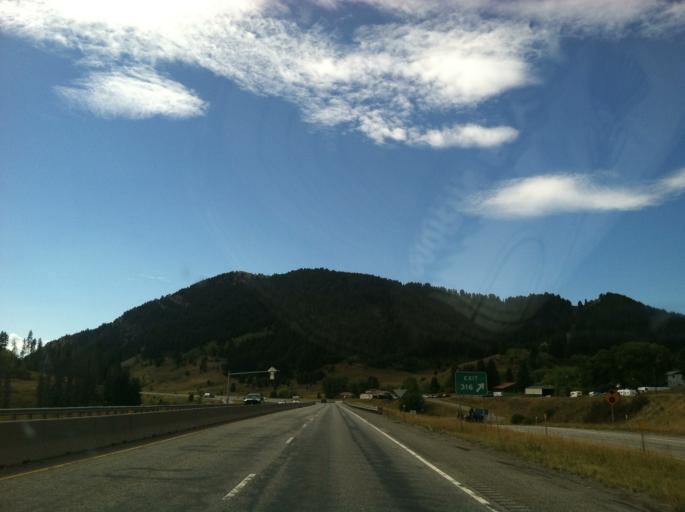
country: US
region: Montana
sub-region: Gallatin County
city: Bozeman
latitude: 45.6467
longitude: -110.8835
